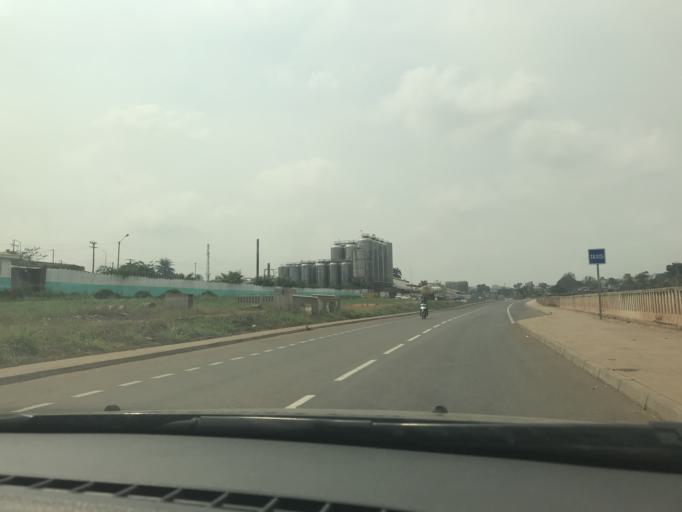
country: CM
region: Centre
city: Yaounde
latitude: 3.8434
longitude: 11.5144
